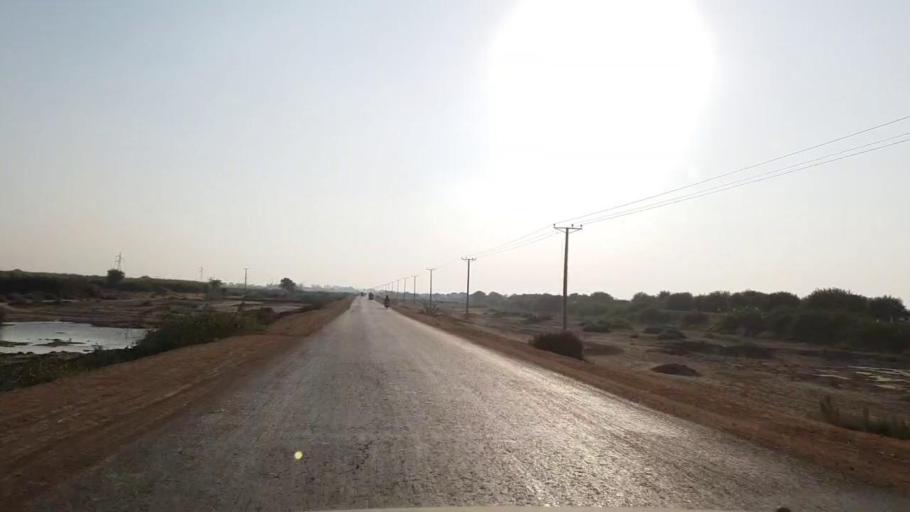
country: PK
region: Sindh
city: Mirpur Batoro
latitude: 24.7562
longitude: 68.2702
